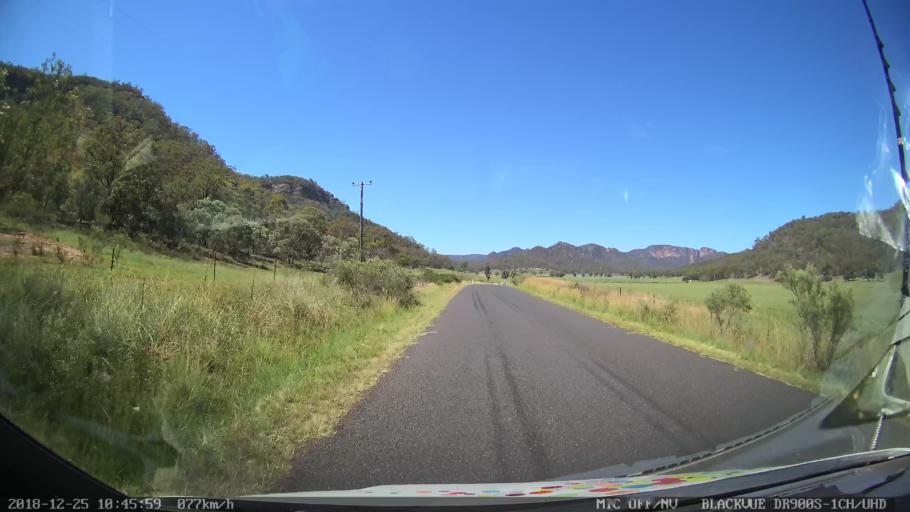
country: AU
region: New South Wales
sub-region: Upper Hunter Shire
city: Merriwa
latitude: -32.4392
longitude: 150.2873
